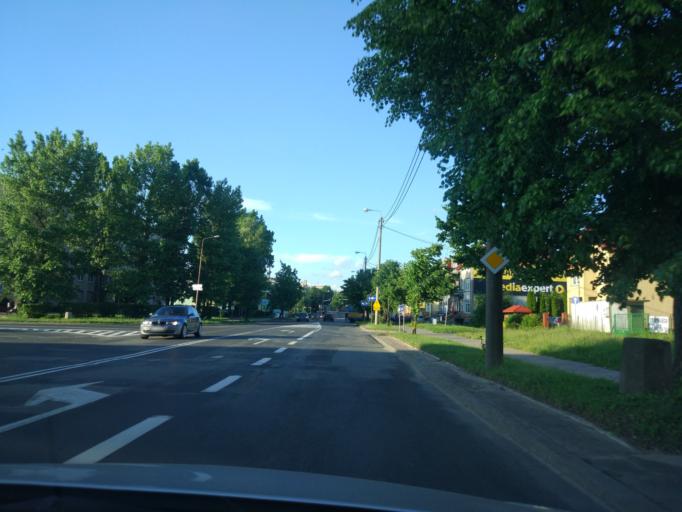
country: PL
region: Lodz Voivodeship
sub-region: Powiat kutnowski
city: Kutno
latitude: 52.2260
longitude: 19.3649
